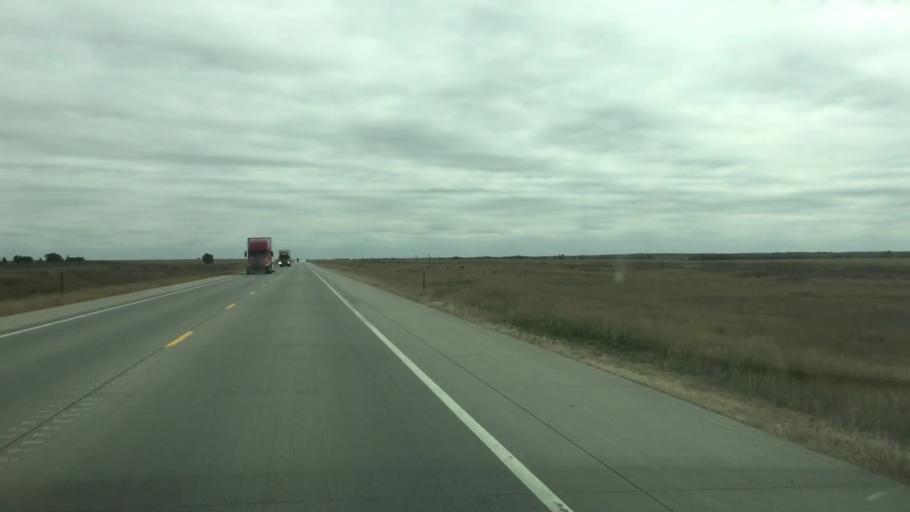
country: US
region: Colorado
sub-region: Kiowa County
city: Eads
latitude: 38.7791
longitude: -102.8956
